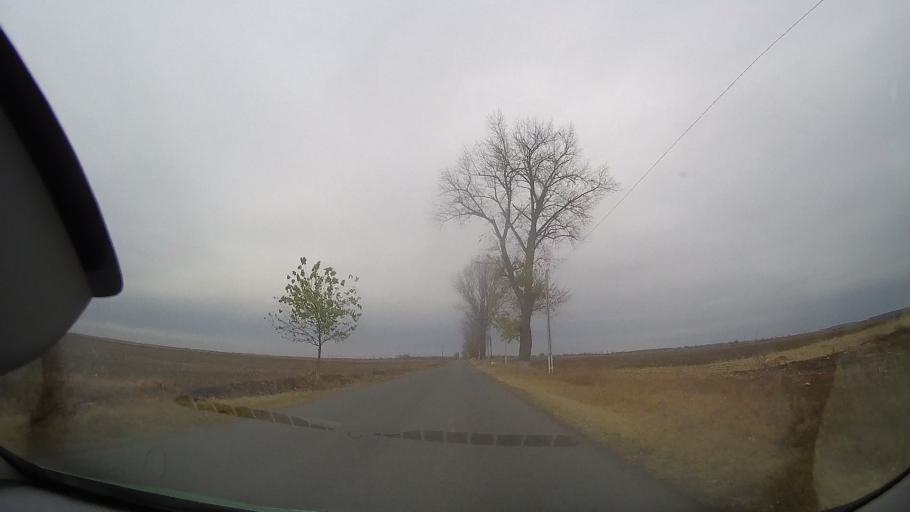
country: RO
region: Braila
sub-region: Comuna Budesti
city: Tataru
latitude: 44.8667
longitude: 27.4271
